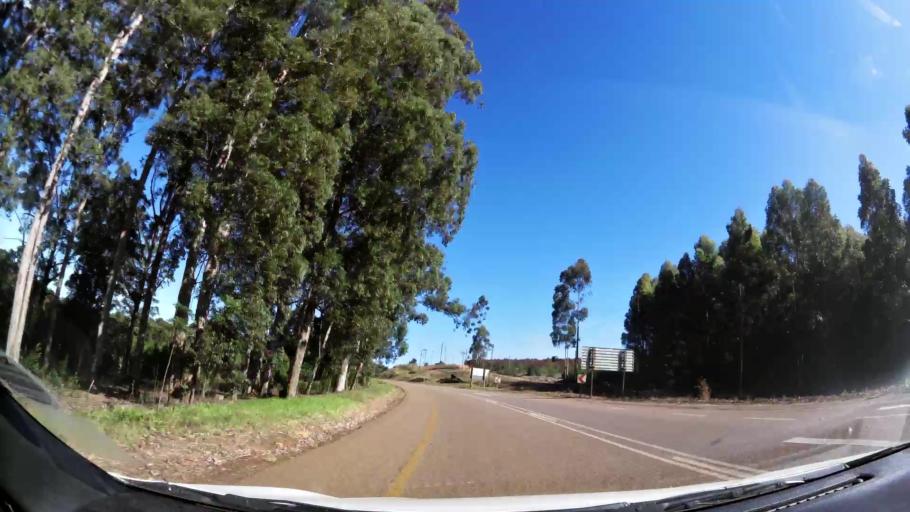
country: ZA
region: Limpopo
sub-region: Capricorn District Municipality
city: Mankoeng
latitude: -23.9158
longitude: 29.9604
